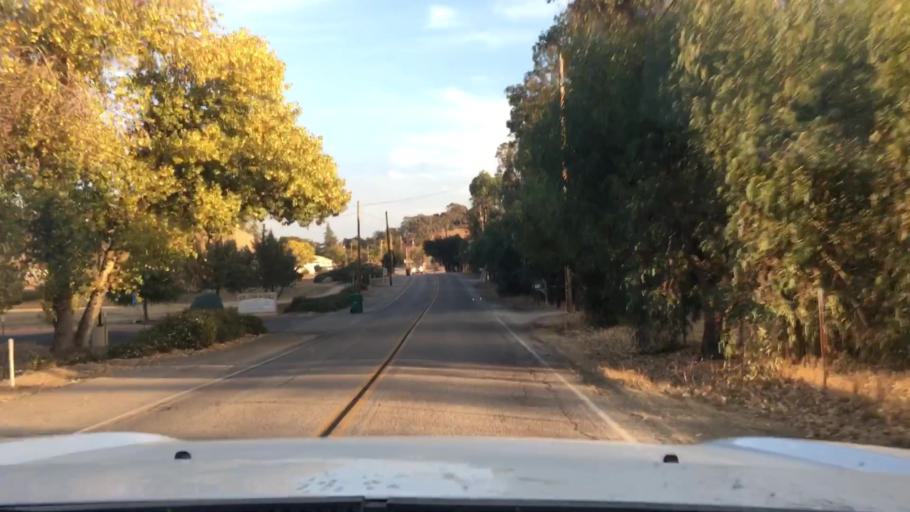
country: US
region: California
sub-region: San Luis Obispo County
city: Atascadero
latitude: 35.4609
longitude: -120.6727
